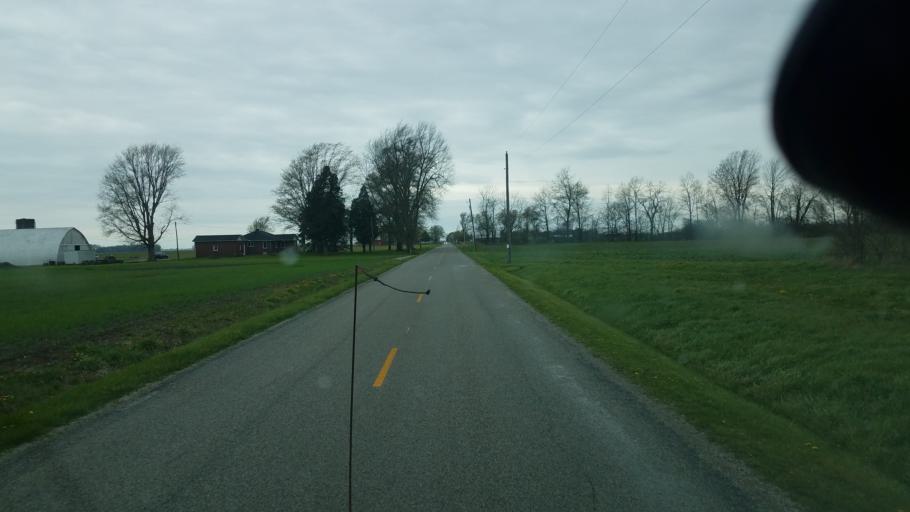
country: US
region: Ohio
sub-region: Marion County
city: Marion
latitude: 40.6520
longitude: -83.0078
